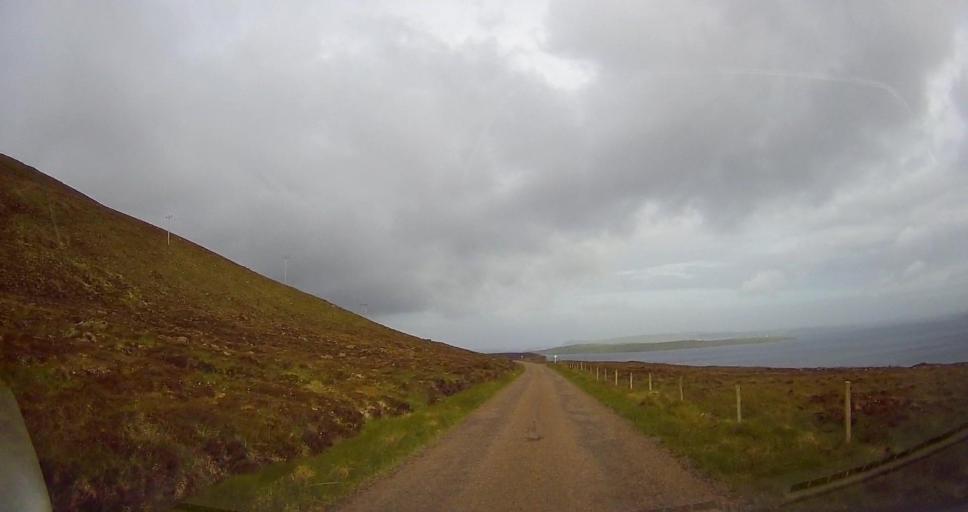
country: GB
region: Scotland
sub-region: Orkney Islands
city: Stromness
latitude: 58.8873
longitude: -3.2526
